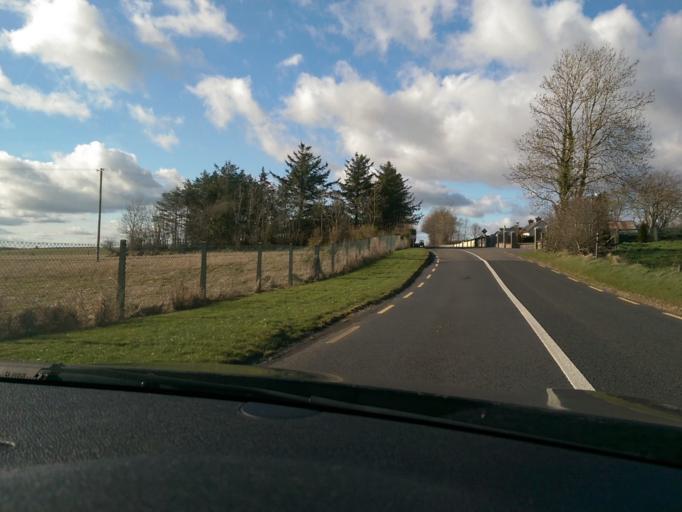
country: IE
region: Connaught
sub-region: Roscommon
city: Castlerea
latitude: 53.5837
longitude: -8.5634
